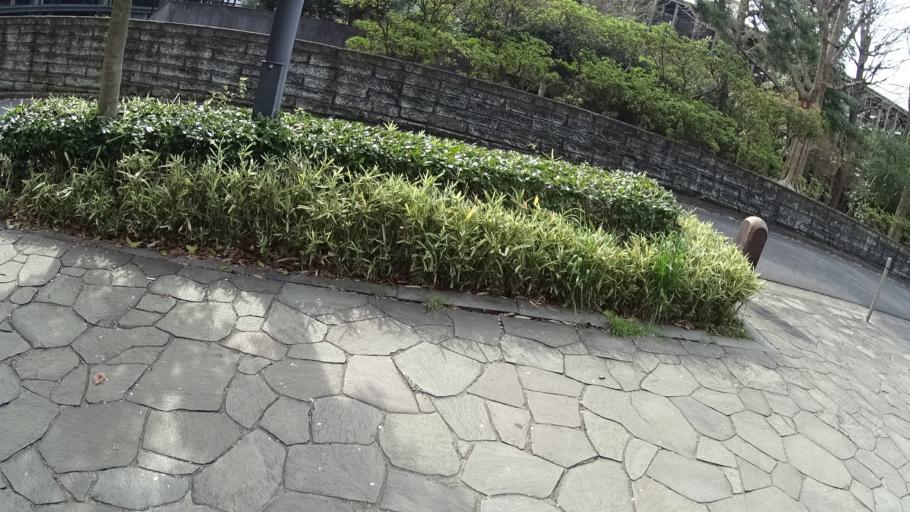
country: JP
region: Kanagawa
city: Yokohama
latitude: 35.4526
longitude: 139.6256
